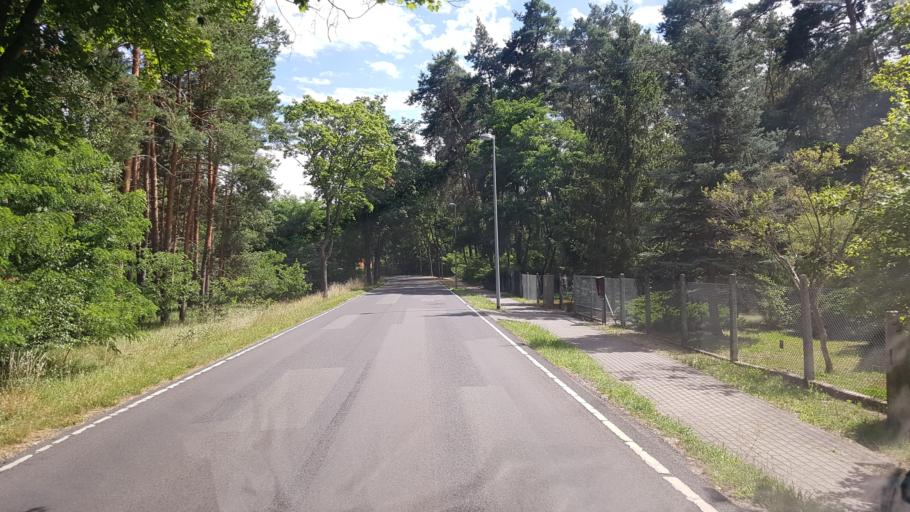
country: DE
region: Brandenburg
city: Luckenwalde
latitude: 52.1214
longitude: 13.1897
